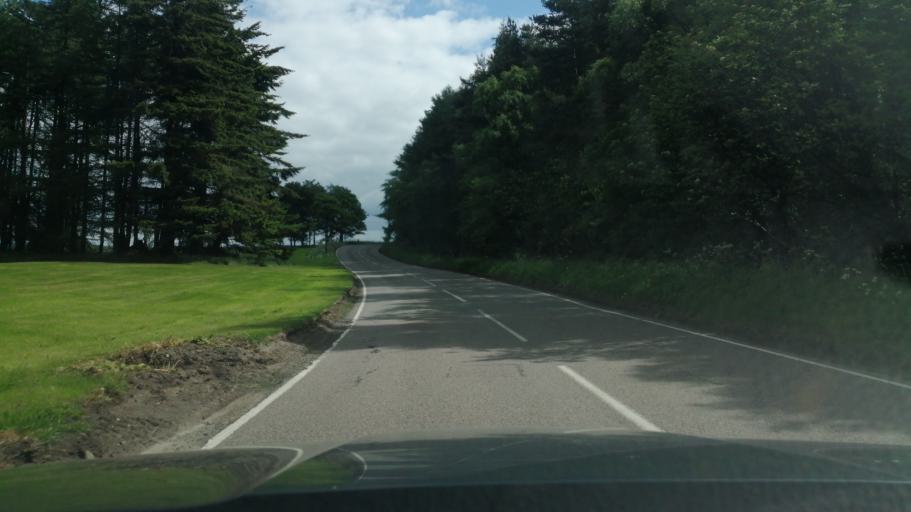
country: GB
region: Scotland
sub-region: Moray
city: Fochabers
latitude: 57.5474
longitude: -3.1115
